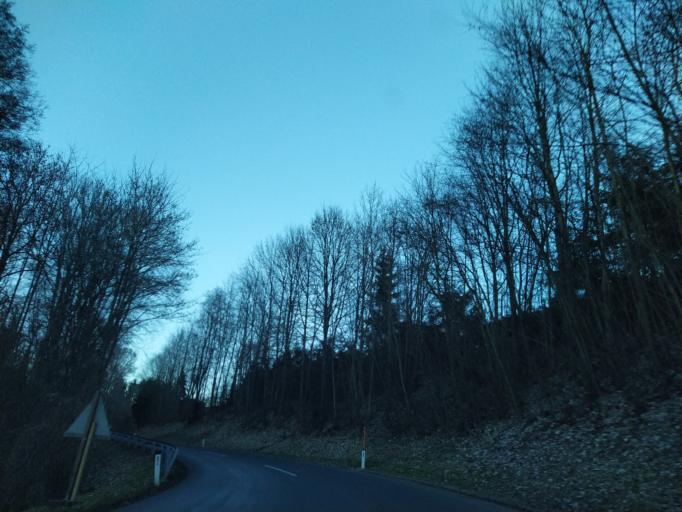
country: AT
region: Upper Austria
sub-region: Politischer Bezirk Urfahr-Umgebung
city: Kirchschlag bei Linz
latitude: 48.3919
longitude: 14.2879
